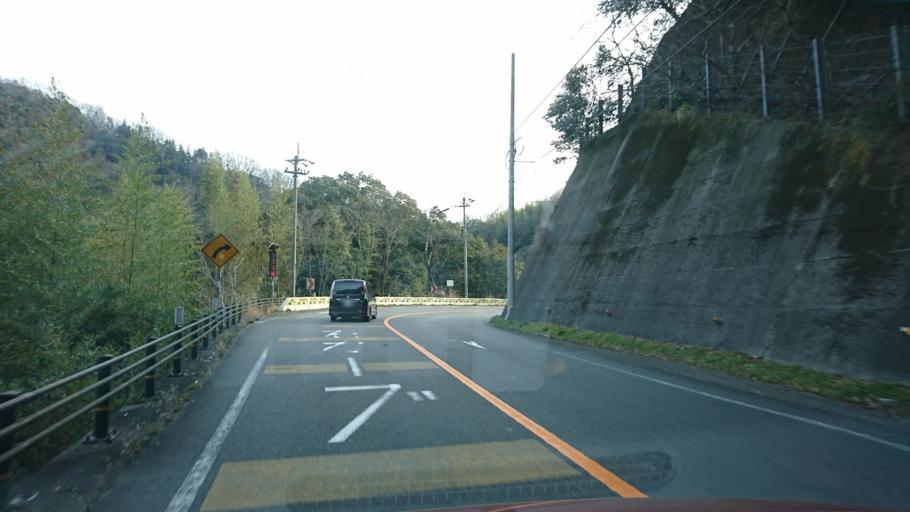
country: JP
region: Ehime
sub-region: Shikoku-chuo Shi
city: Matsuyama
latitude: 33.8914
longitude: 132.8390
